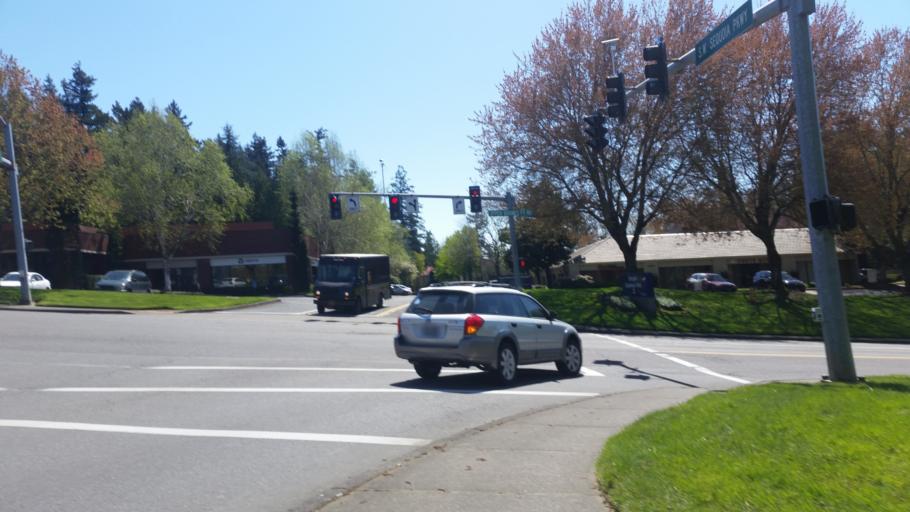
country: US
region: Oregon
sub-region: Washington County
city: Durham
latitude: 45.4063
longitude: -122.7472
